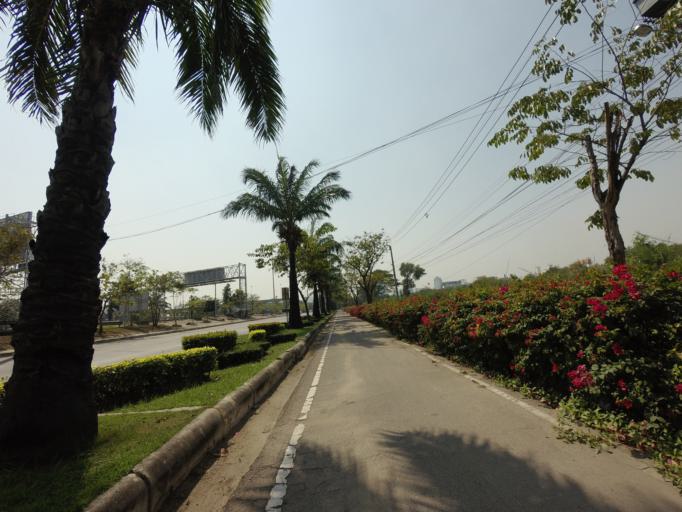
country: TH
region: Bangkok
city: Huai Khwang
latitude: 13.7554
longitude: 100.5945
